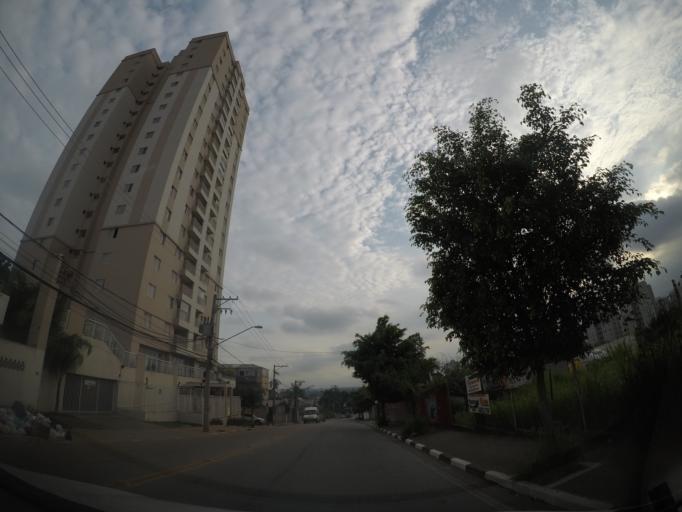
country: BR
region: Sao Paulo
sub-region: Guarulhos
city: Guarulhos
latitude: -23.4615
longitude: -46.5117
